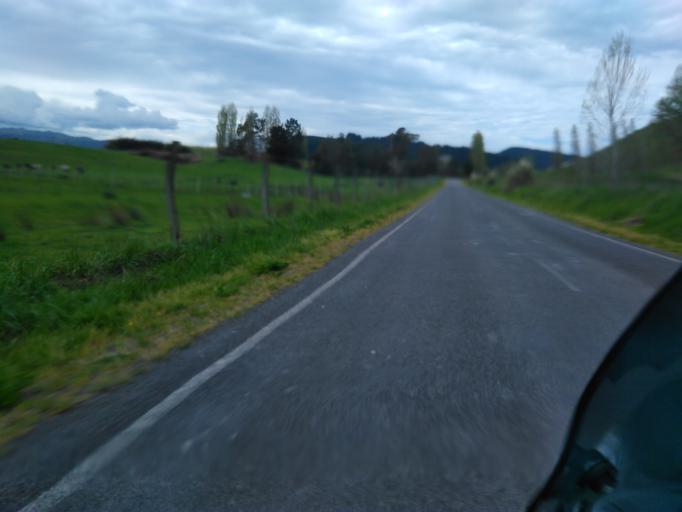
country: NZ
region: Hawke's Bay
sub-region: Wairoa District
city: Wairoa
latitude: -38.8983
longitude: 177.4646
